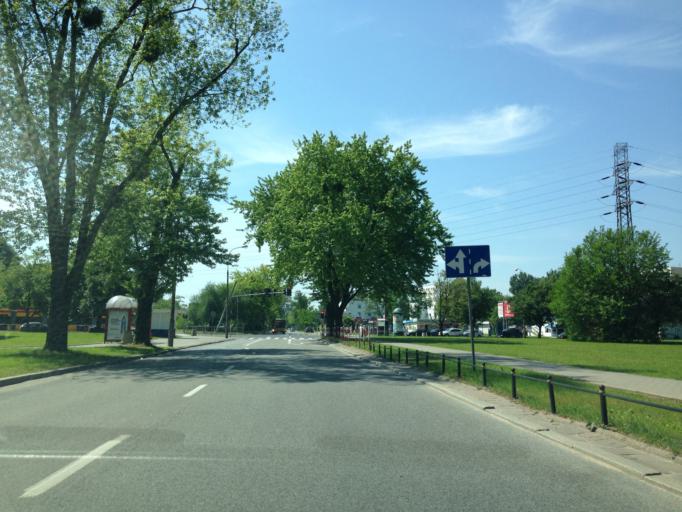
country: PL
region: Masovian Voivodeship
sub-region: Warszawa
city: Zoliborz
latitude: 52.2651
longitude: 20.9729
